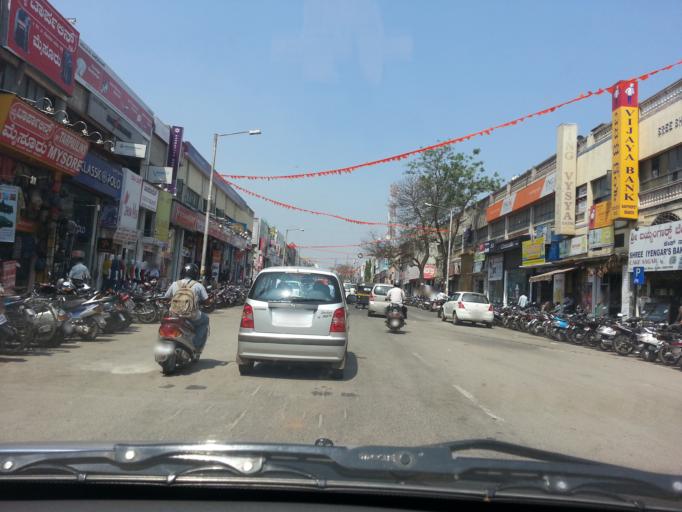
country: IN
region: Karnataka
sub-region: Mysore
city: Mysore
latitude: 12.3088
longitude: 76.6520
